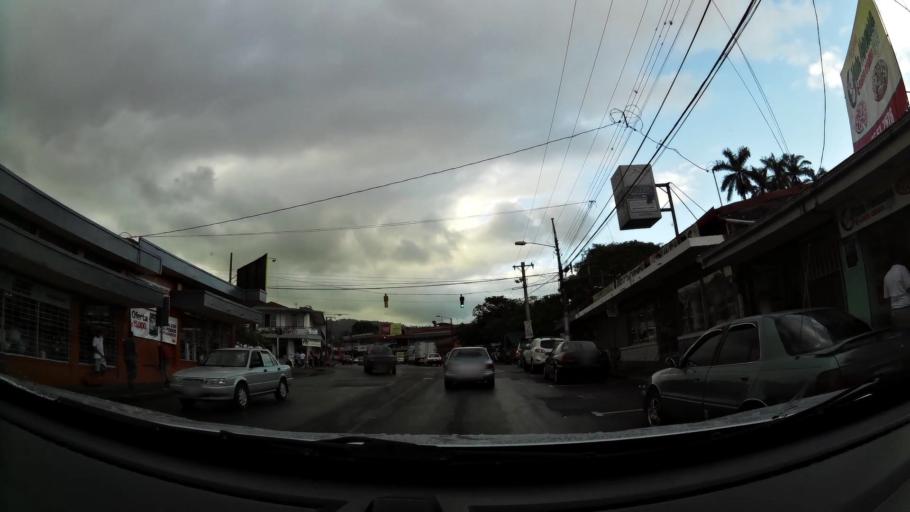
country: CR
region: Cartago
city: Turrialba
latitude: 9.9033
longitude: -83.6831
